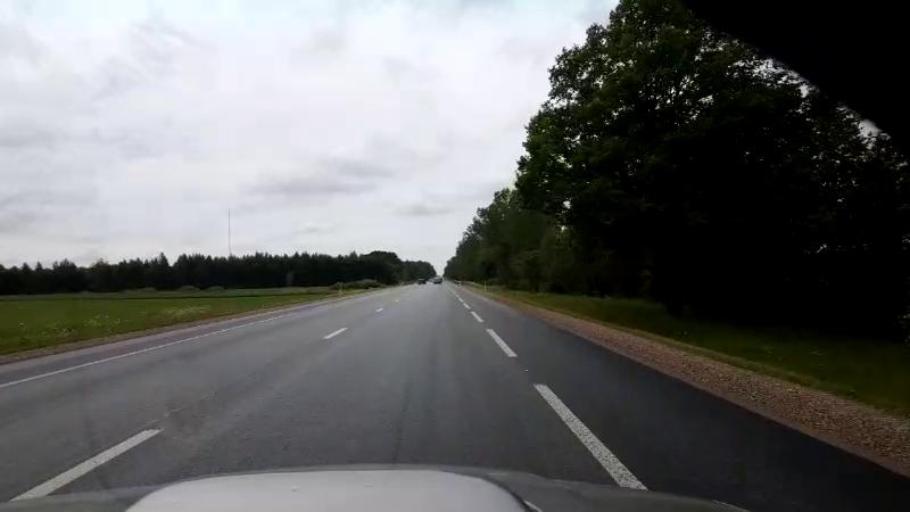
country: LV
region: Lecava
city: Iecava
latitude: 56.6757
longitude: 24.2365
